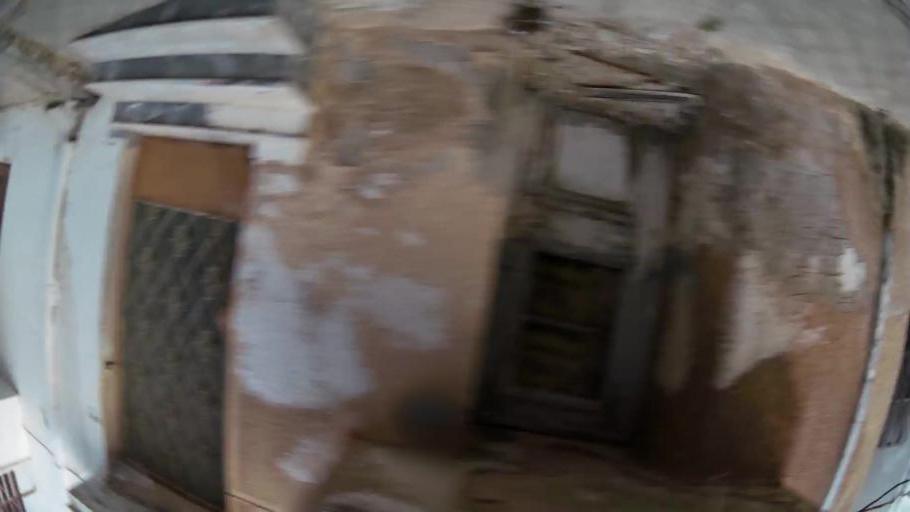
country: GR
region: Attica
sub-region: Nomarchia Athinas
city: Dhafni
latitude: 37.9549
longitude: 23.7285
